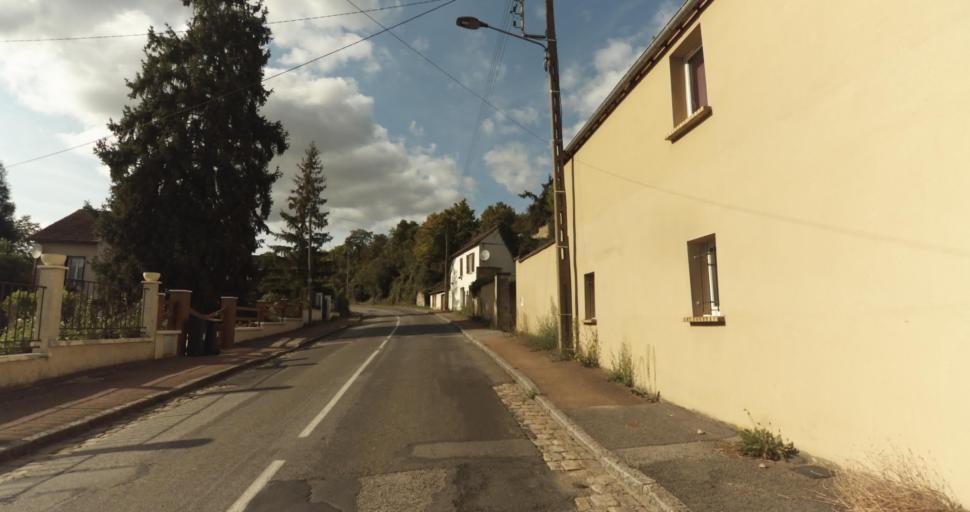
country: FR
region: Haute-Normandie
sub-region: Departement de l'Eure
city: Ivry-la-Bataille
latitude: 48.8854
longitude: 1.4549
